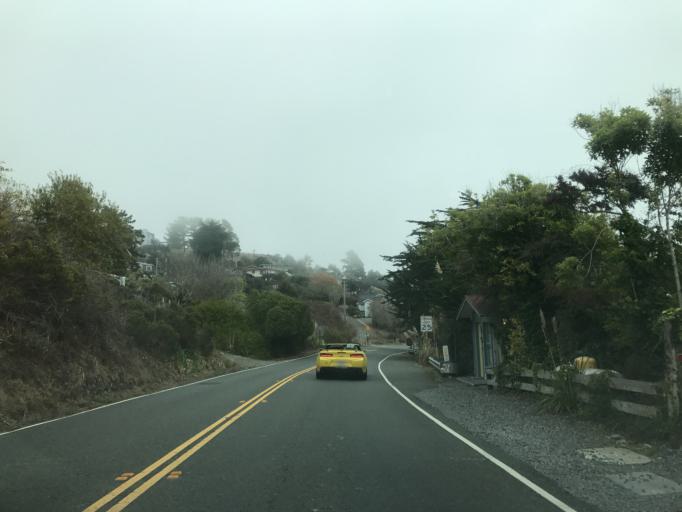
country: US
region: California
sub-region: Sonoma County
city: Monte Rio
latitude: 38.4507
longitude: -123.1213
